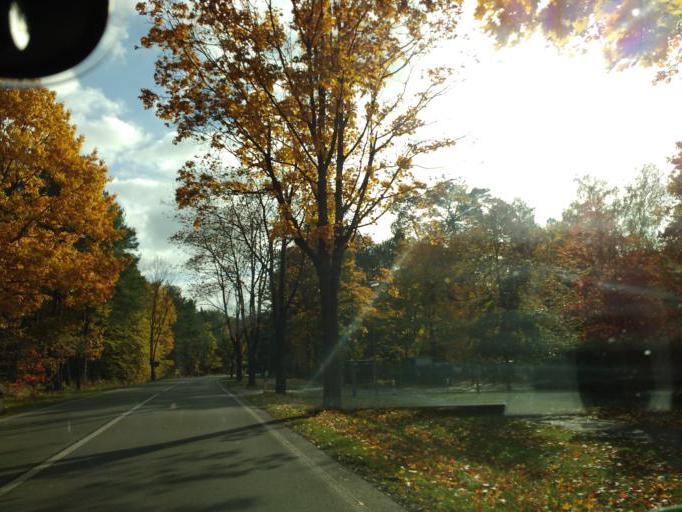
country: DE
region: Brandenburg
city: Grunheide
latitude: 52.4144
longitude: 13.8259
